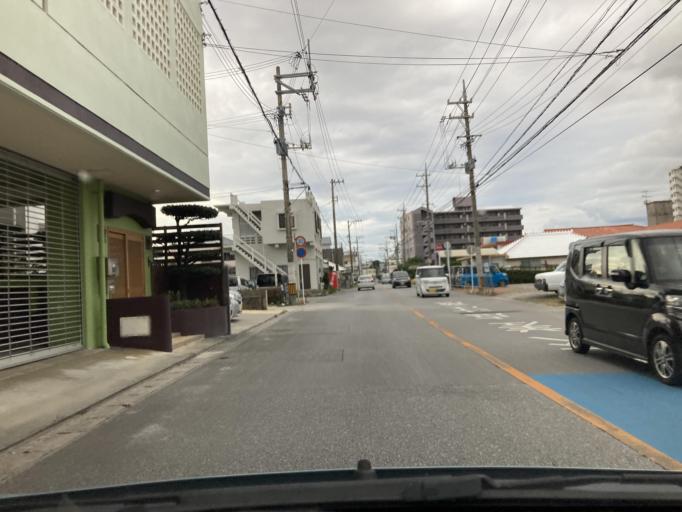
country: JP
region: Okinawa
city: Ginowan
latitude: 26.2698
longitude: 127.7387
